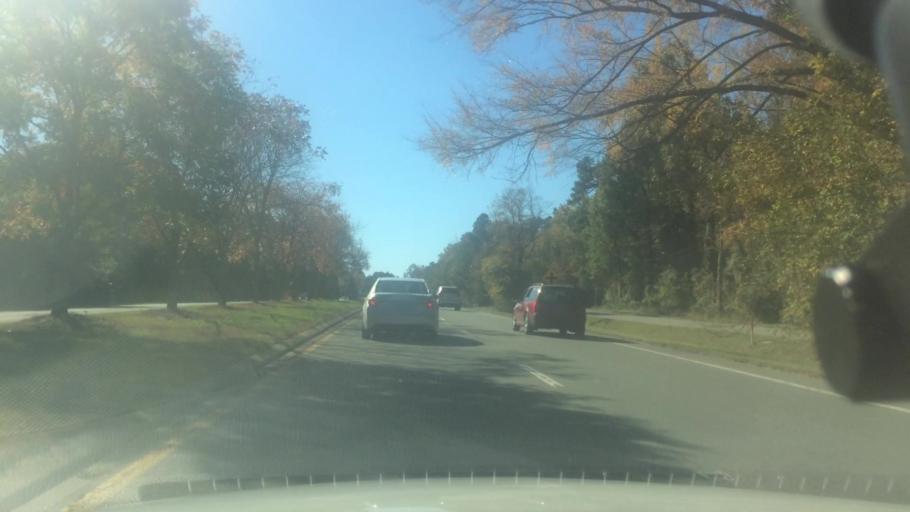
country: US
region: North Carolina
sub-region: Orange County
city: Chapel Hill
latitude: 35.9168
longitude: -79.0264
